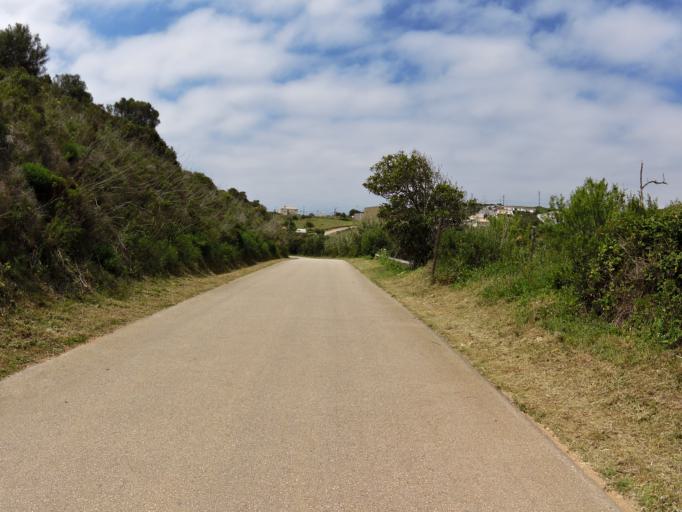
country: PT
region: Faro
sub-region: Vila do Bispo
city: Vila do Bispo
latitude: 37.0679
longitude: -8.8721
